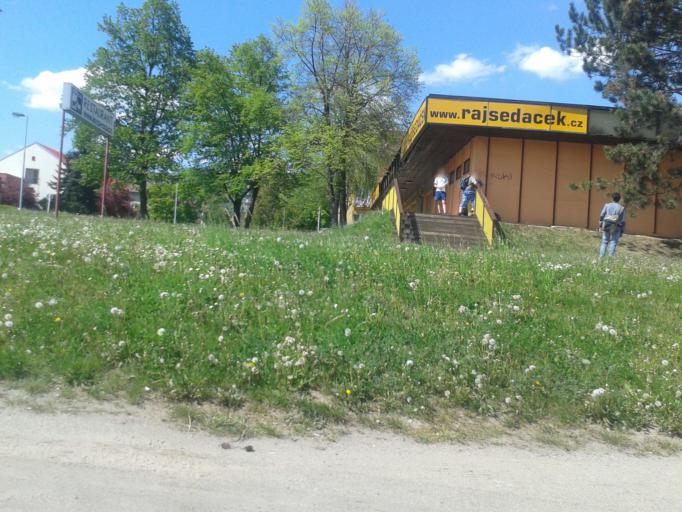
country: CZ
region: Central Bohemia
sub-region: Okres Beroun
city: Kraluv Dvur
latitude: 49.9550
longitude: 14.0531
